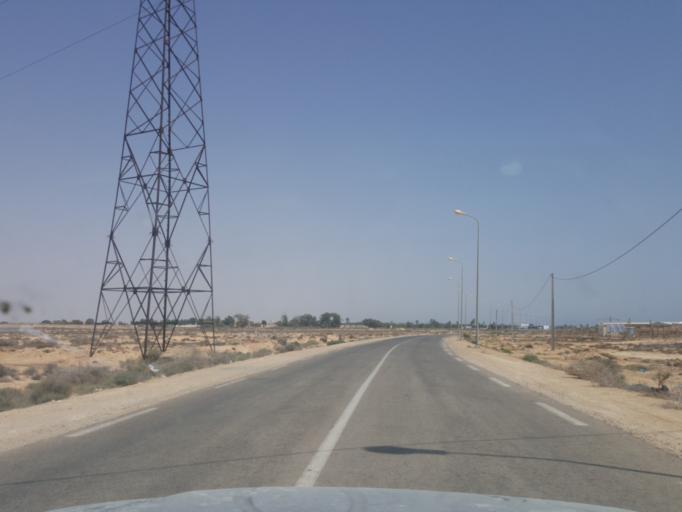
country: TN
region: Qabis
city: Gabes
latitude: 33.9763
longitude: 10.0026
